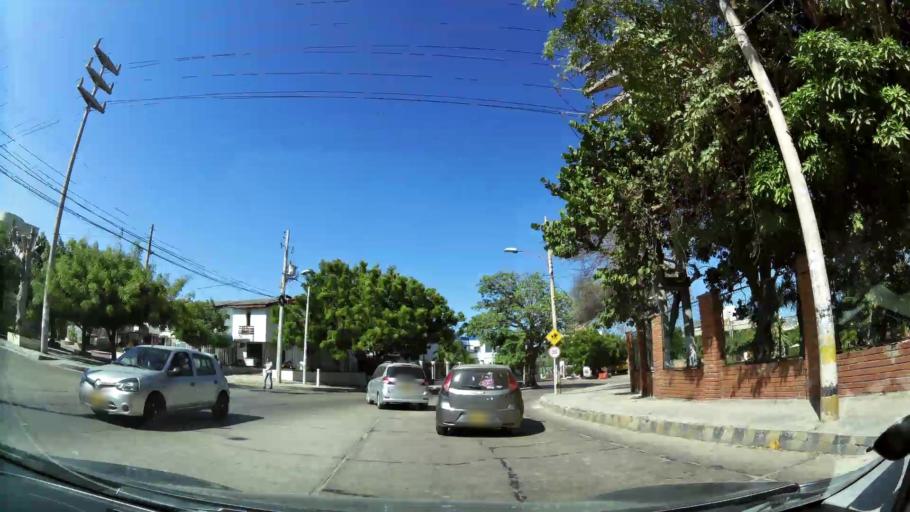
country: CO
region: Atlantico
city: Barranquilla
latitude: 10.9969
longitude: -74.7912
